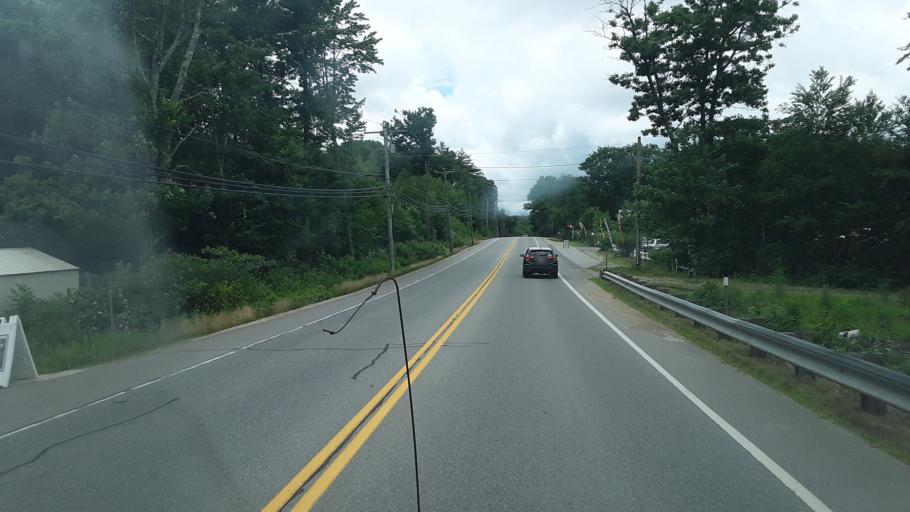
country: US
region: New Hampshire
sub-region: Rockingham County
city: Northwood
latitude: 43.2204
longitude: -71.2285
